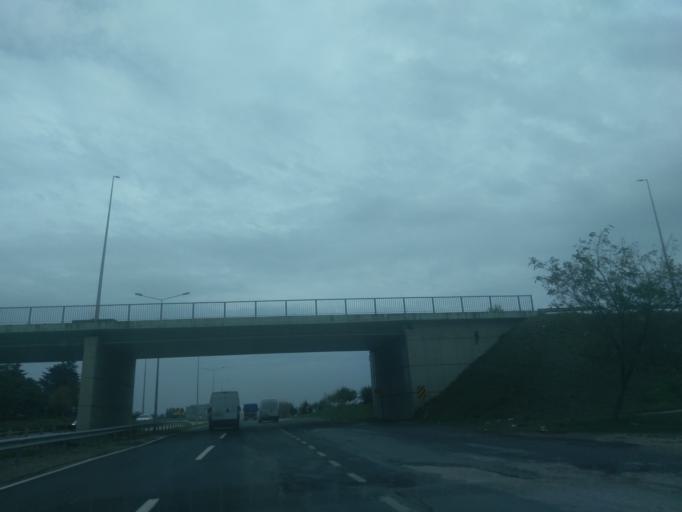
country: TR
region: Istanbul
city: Silivri
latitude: 41.0809
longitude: 28.2114
